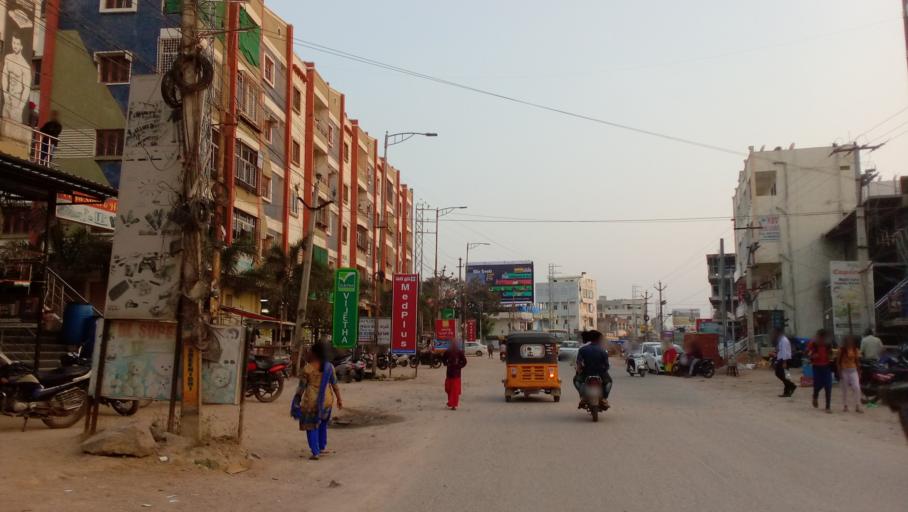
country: IN
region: Telangana
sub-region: Medak
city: Serilingampalle
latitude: 17.5205
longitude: 78.2996
